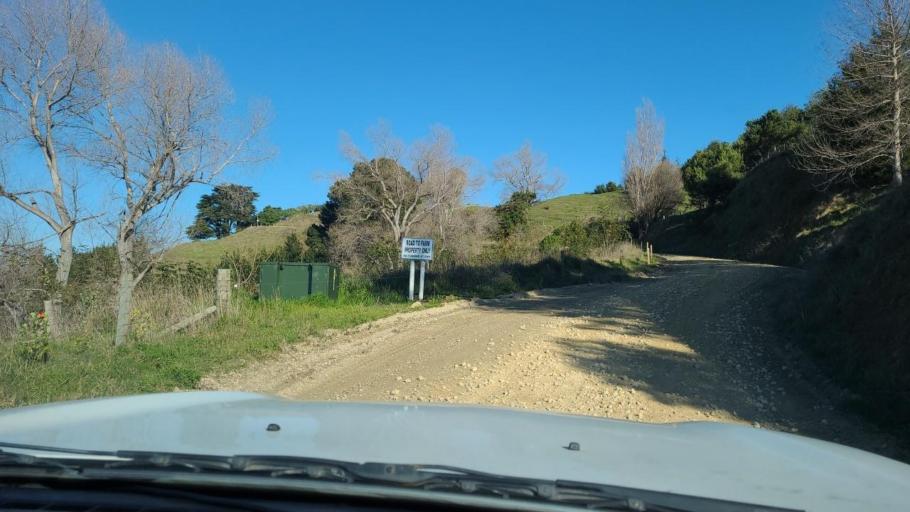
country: NZ
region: Hawke's Bay
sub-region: Hastings District
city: Hastings
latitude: -39.7916
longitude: 176.9759
